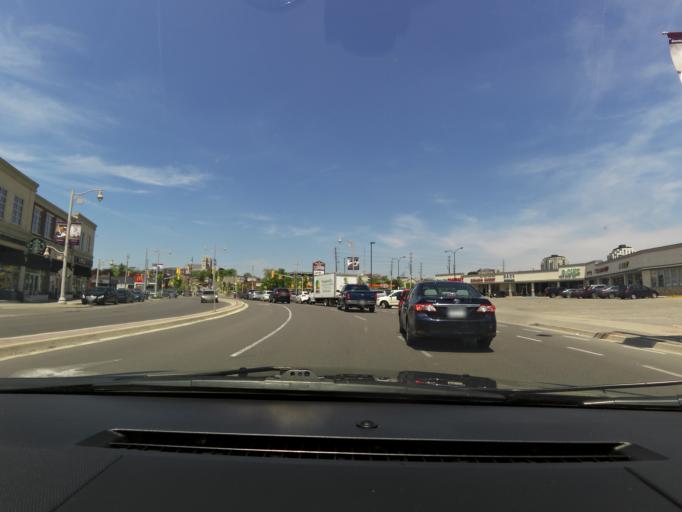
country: CA
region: Ontario
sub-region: Wellington County
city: Guelph
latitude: 43.5403
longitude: -80.2436
